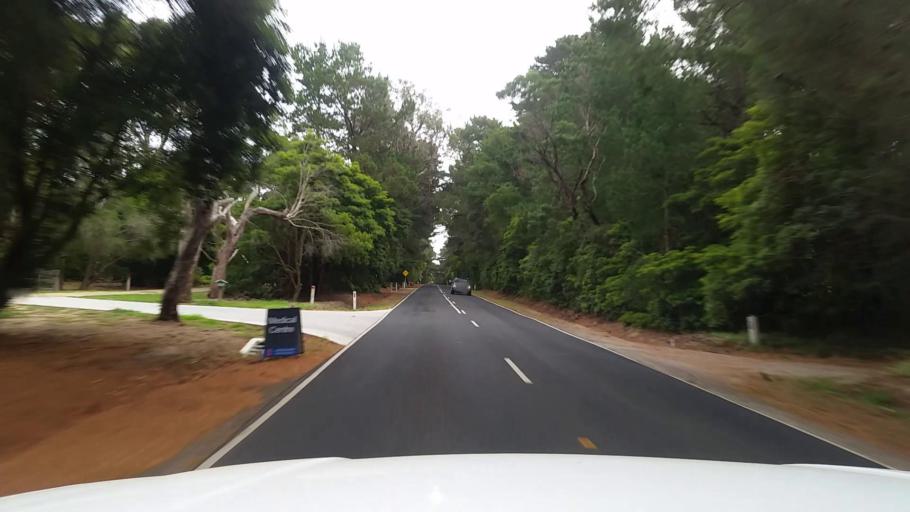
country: AU
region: Victoria
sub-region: Mornington Peninsula
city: Balnarring
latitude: -38.3694
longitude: 145.1225
